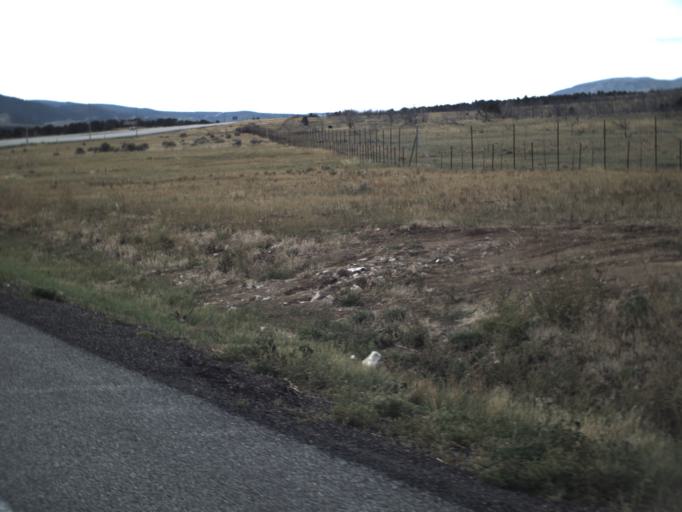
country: US
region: Utah
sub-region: Beaver County
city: Beaver
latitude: 38.5705
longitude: -112.6053
